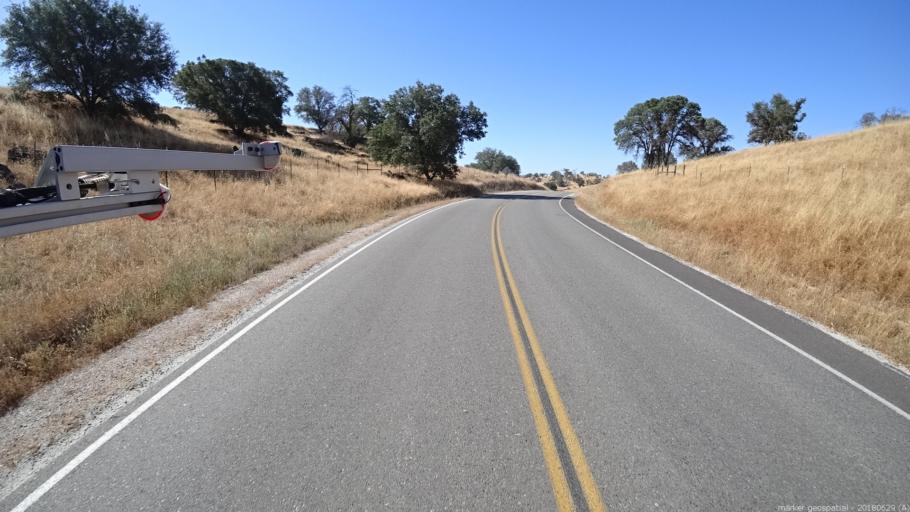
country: US
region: California
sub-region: Madera County
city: Yosemite Lakes
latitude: 37.0782
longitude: -119.7940
